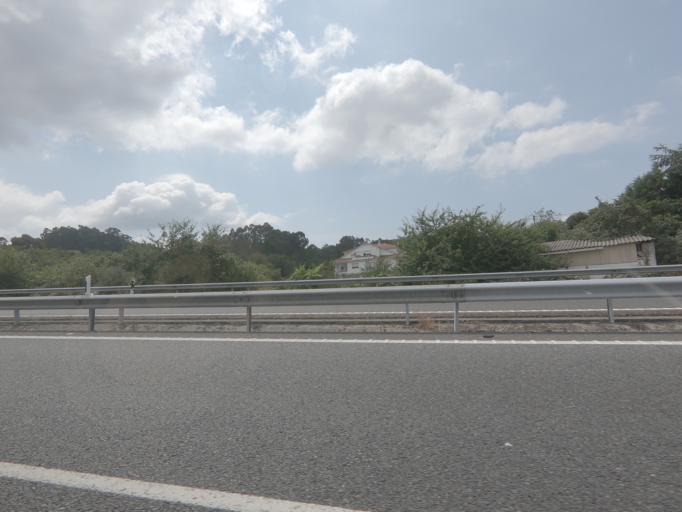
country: ES
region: Galicia
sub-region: Provincia de Pontevedra
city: Tui
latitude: 42.0554
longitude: -8.6546
